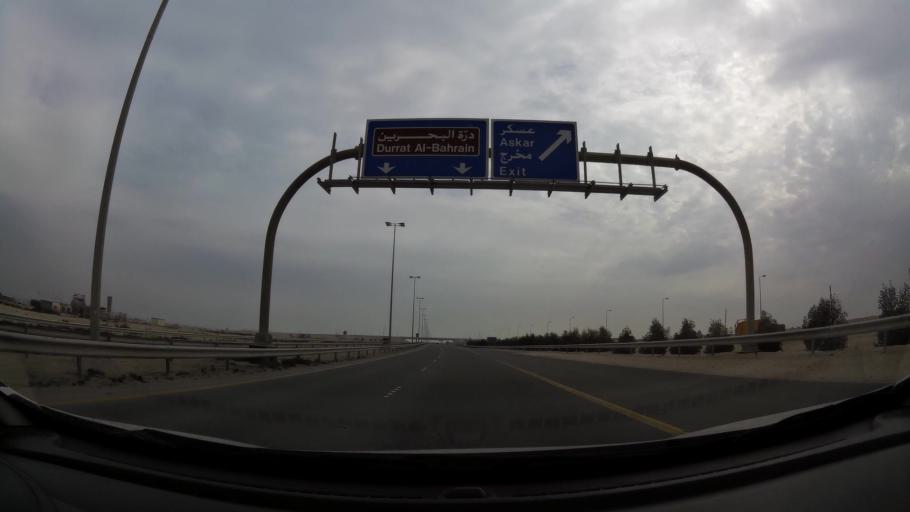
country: BH
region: Northern
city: Ar Rifa'
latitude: 26.0541
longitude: 50.6067
